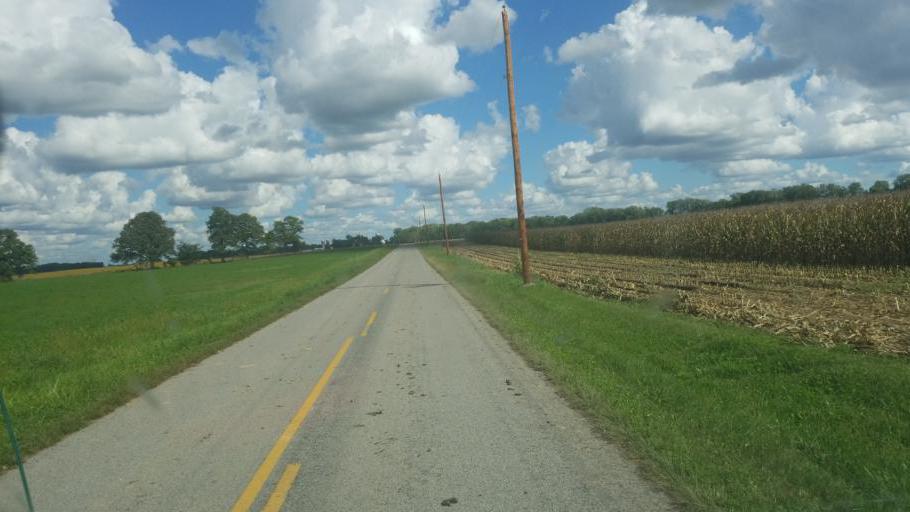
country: US
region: Ohio
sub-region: Hardin County
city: Kenton
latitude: 40.5031
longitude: -83.5471
